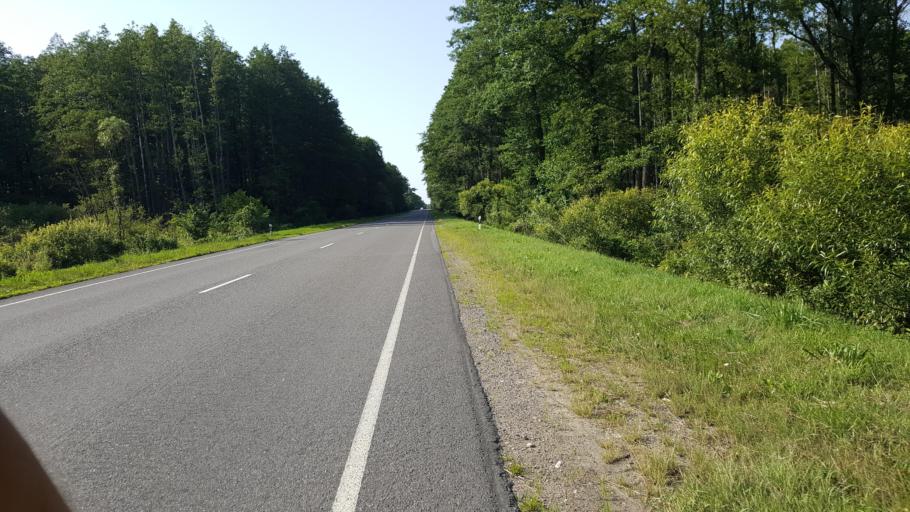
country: BY
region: Brest
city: Zhabinka
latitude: 52.2818
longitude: 23.9477
